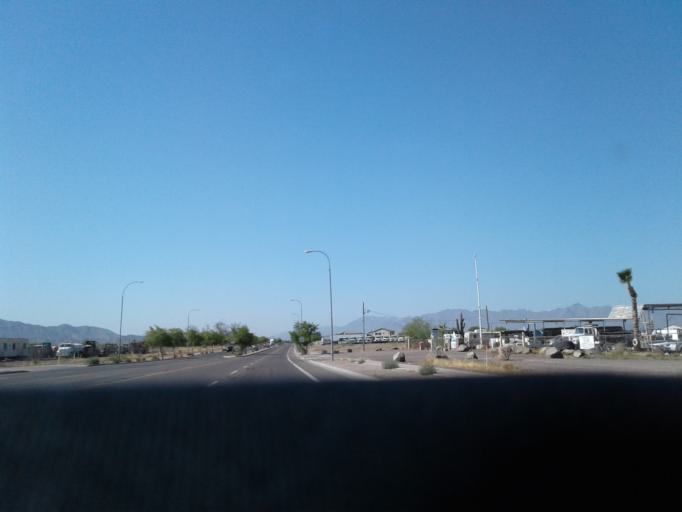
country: US
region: Arizona
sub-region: Maricopa County
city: Laveen
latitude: 33.4024
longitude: -112.1685
